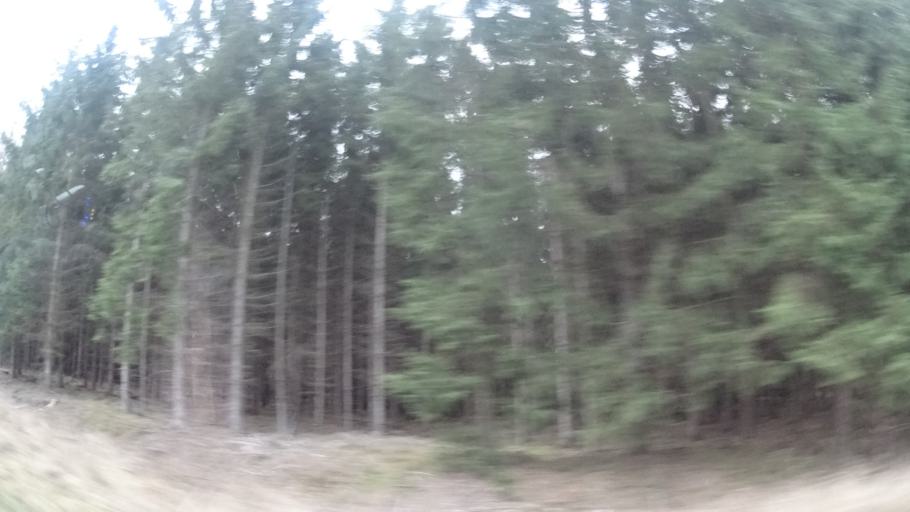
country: DE
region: Thuringia
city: Auma
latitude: 50.7086
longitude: 11.8869
